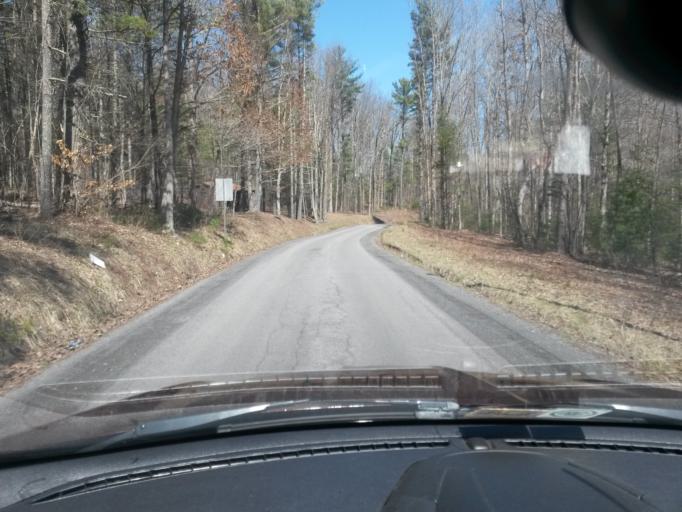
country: US
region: West Virginia
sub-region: Greenbrier County
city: White Sulphur Springs
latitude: 37.6383
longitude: -80.3373
